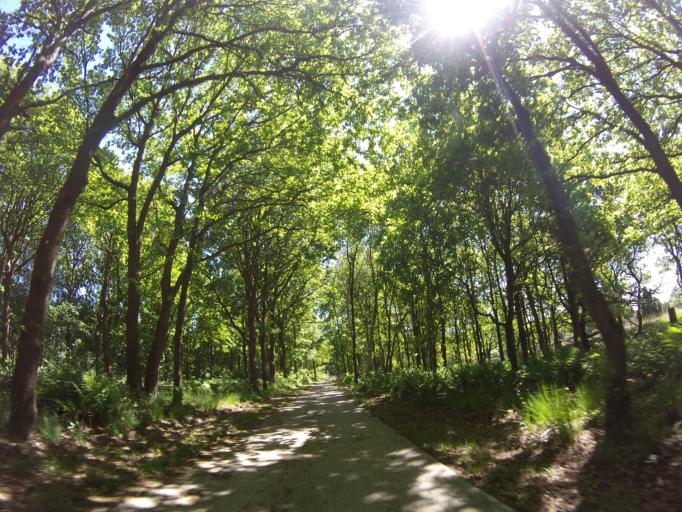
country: NL
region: Drenthe
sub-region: Gemeente Coevorden
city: Dalen
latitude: 52.7930
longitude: 6.6305
